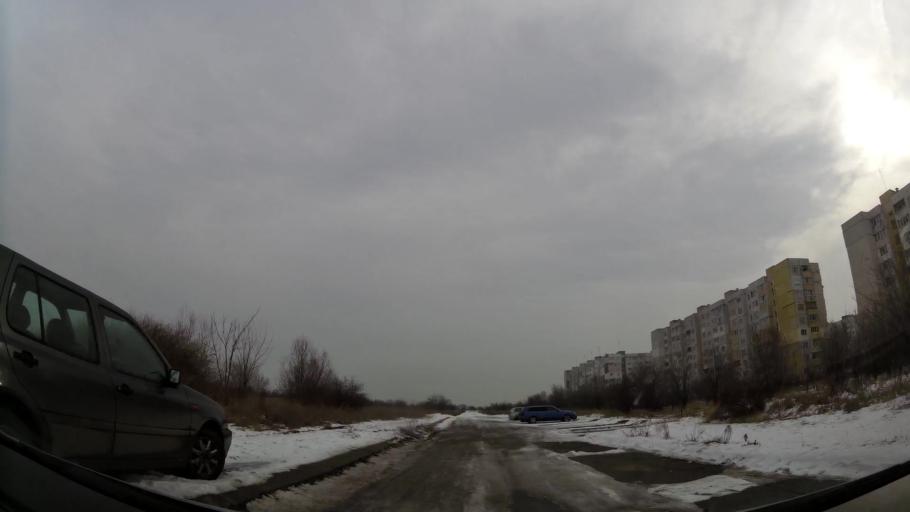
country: BG
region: Sofia-Capital
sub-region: Stolichna Obshtina
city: Sofia
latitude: 42.7148
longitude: 23.3850
